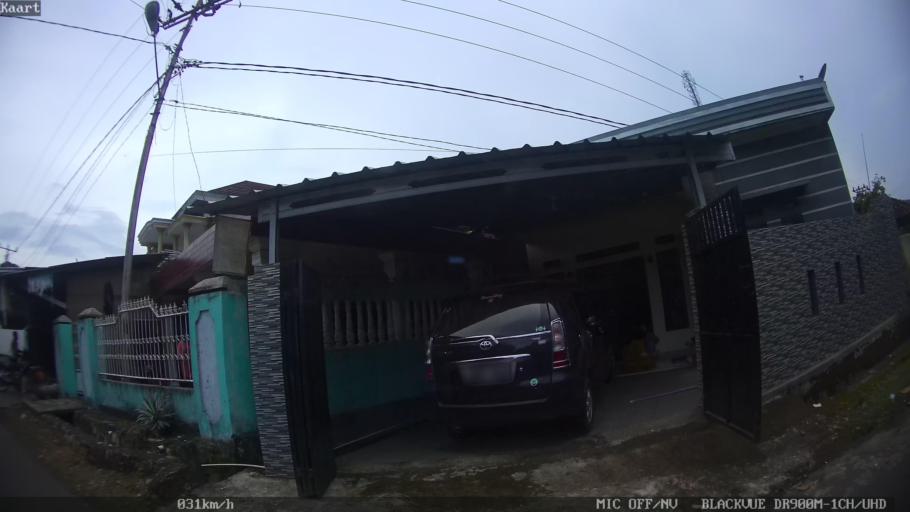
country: ID
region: Lampung
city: Bandarlampung
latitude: -5.4360
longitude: 105.2241
